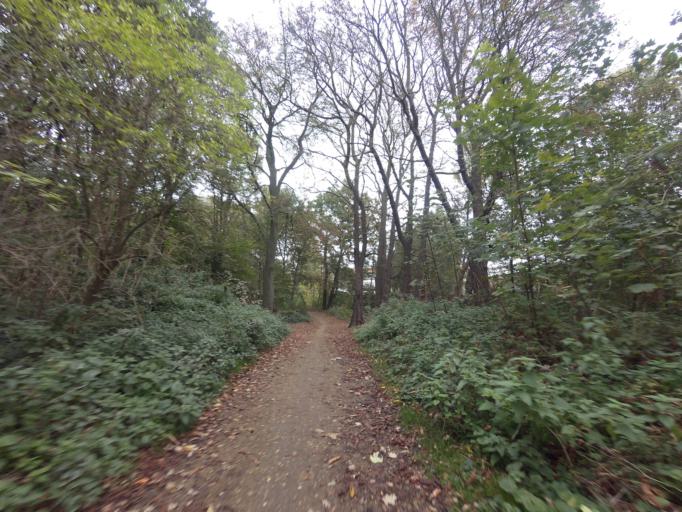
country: BE
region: Flanders
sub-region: Provincie Antwerpen
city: Schoten
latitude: 51.2442
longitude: 4.4558
